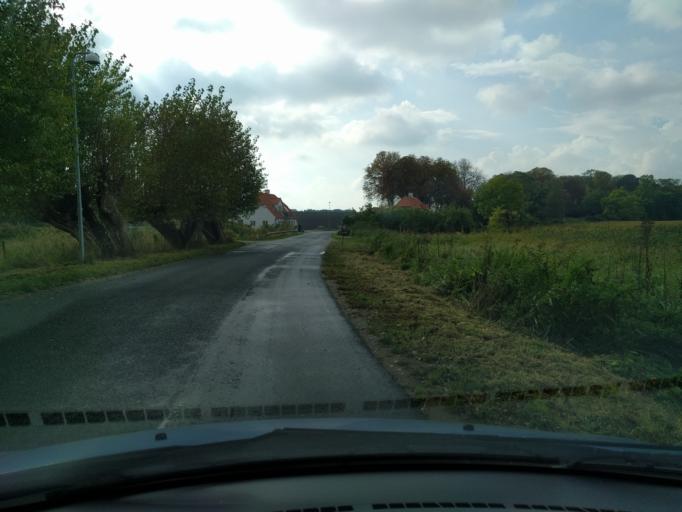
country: DK
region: South Denmark
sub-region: Kerteminde Kommune
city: Munkebo
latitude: 55.4221
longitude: 10.5765
